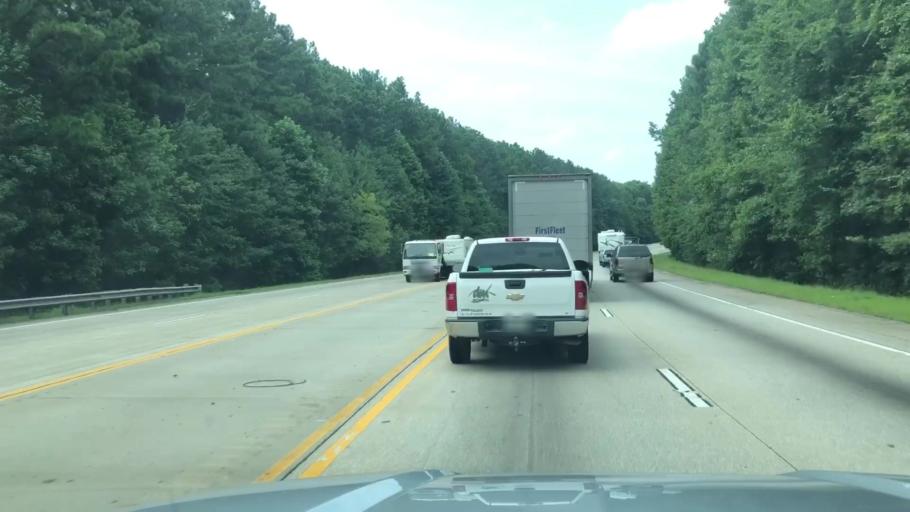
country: US
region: Georgia
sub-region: Douglas County
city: Lithia Springs
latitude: 33.8001
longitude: -84.6490
